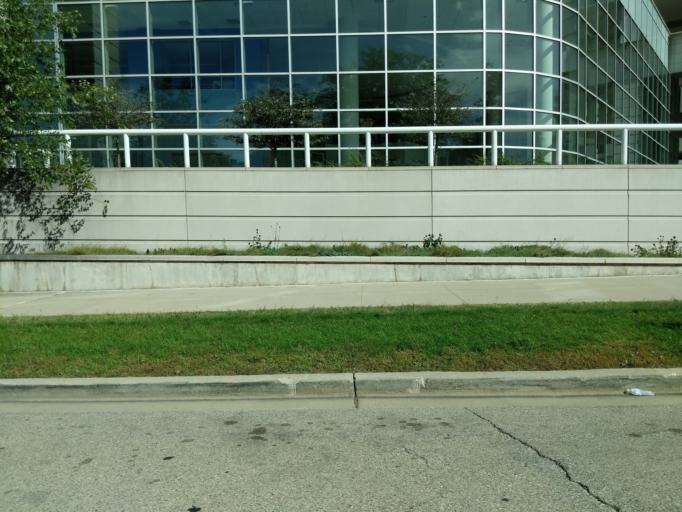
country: US
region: Wisconsin
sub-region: Milwaukee County
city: Shorewood
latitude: 43.0602
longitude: -87.8810
